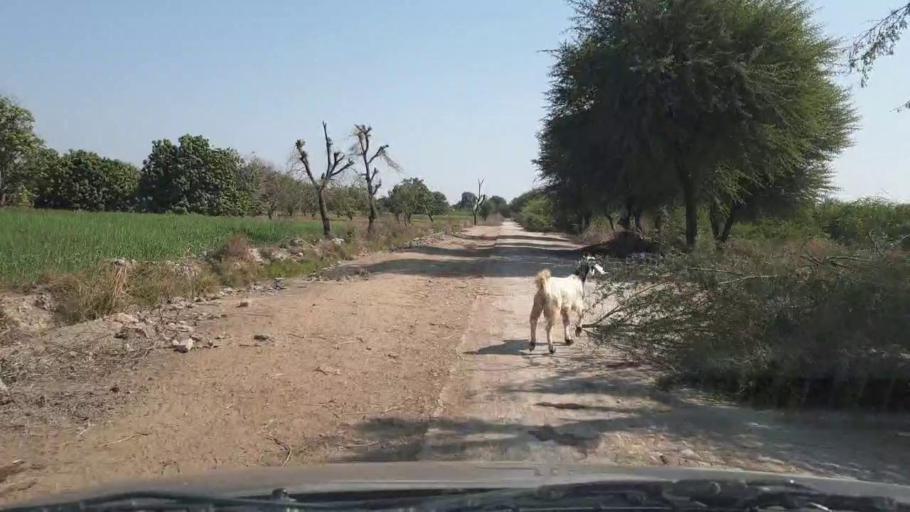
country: PK
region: Sindh
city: Digri
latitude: 25.2020
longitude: 69.2366
